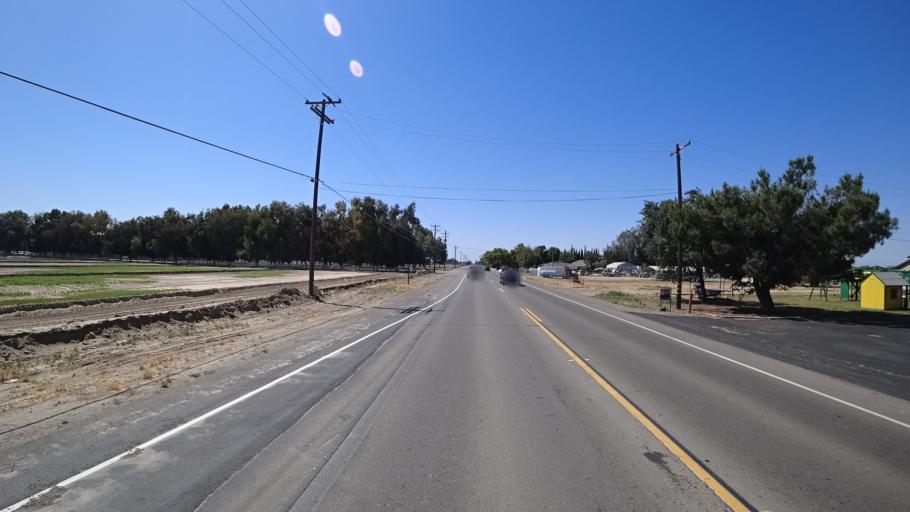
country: US
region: California
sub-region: Kings County
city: Lemoore
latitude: 36.2681
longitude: -119.7809
